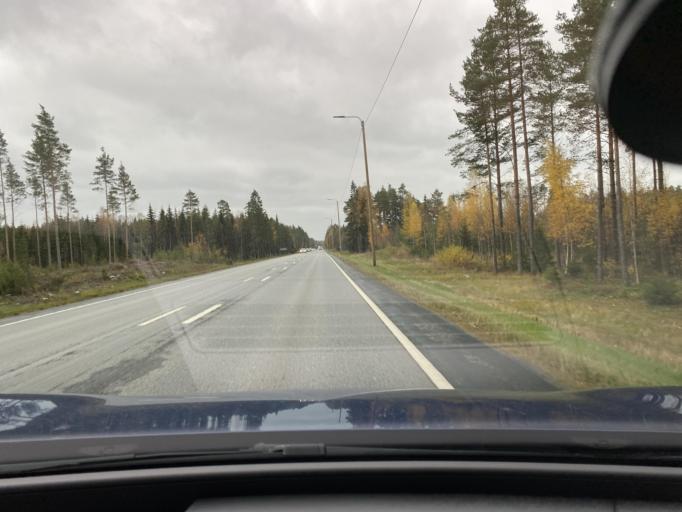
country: FI
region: Varsinais-Suomi
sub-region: Vakka-Suomi
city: Laitila
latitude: 60.9537
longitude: 21.5972
